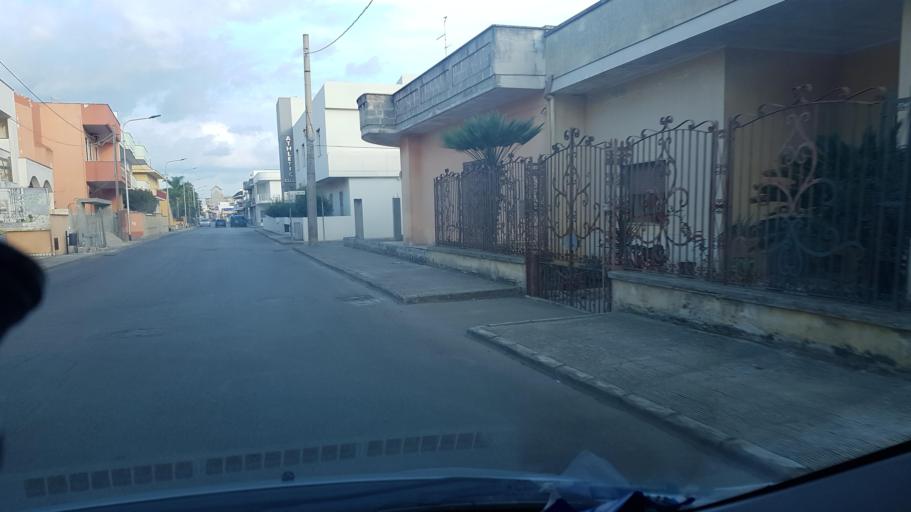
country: IT
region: Apulia
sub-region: Provincia di Lecce
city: Carmiano
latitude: 40.3453
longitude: 18.0364
